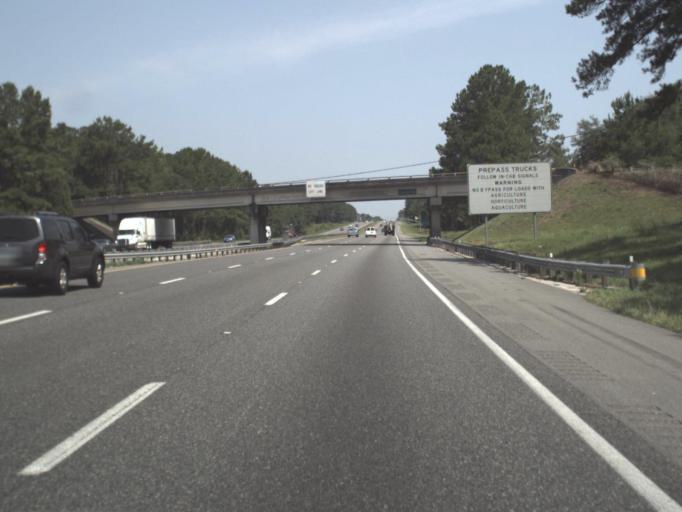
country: US
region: Florida
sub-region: Suwannee County
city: Live Oak
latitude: 30.3716
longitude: -82.8610
